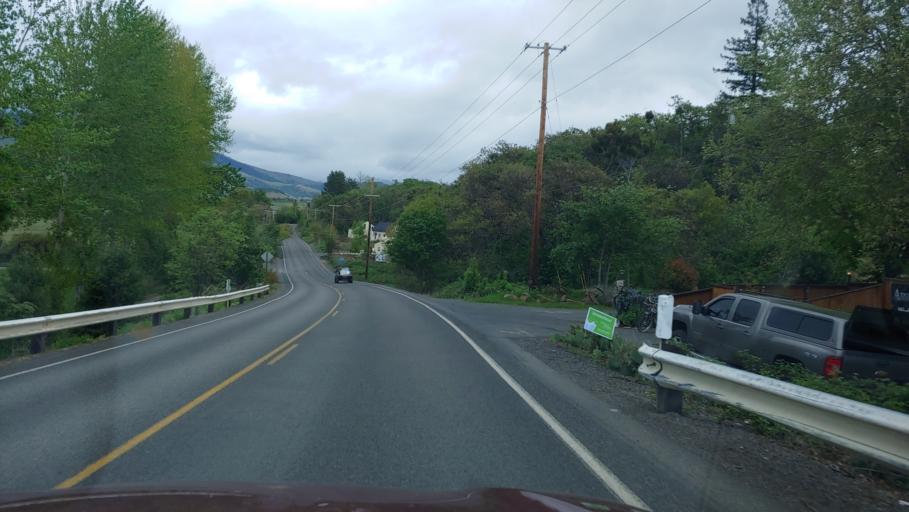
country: US
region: Oregon
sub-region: Jackson County
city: Ashland
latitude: 42.1925
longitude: -122.6698
